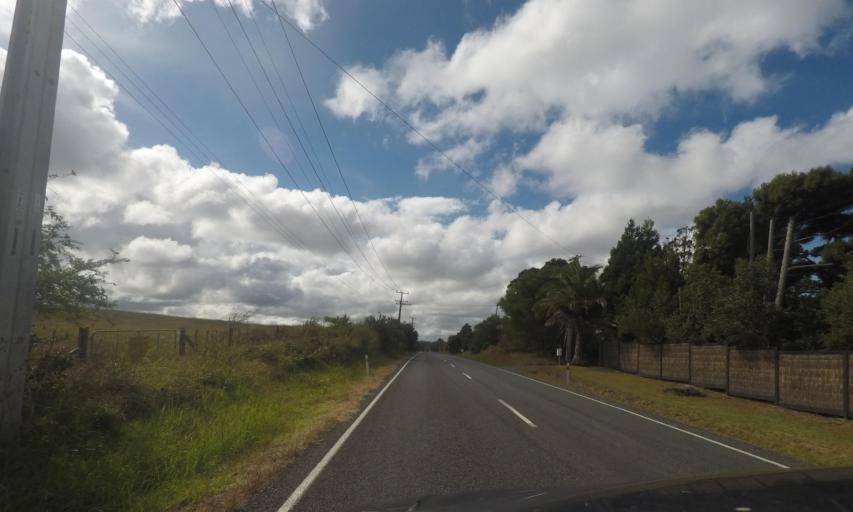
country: NZ
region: Auckland
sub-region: Auckland
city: Rosebank
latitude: -36.7842
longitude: 174.6435
